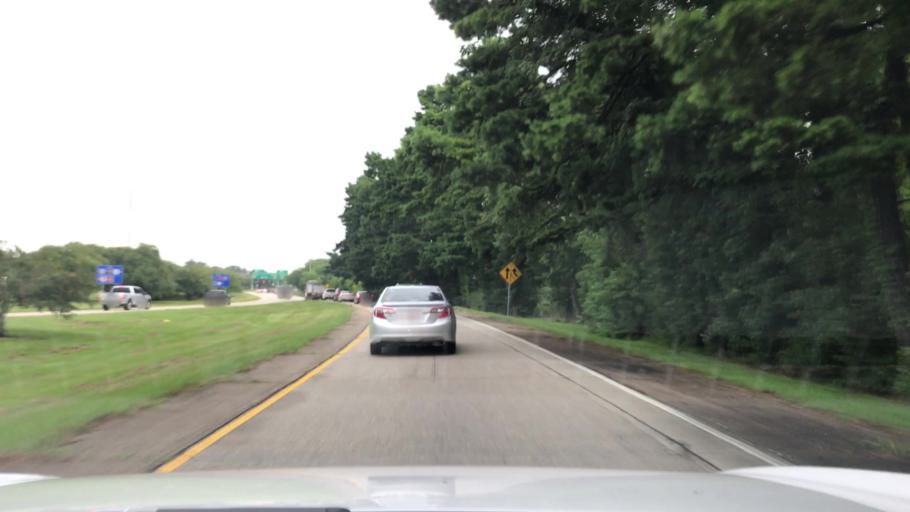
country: US
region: Louisiana
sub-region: East Baton Rouge Parish
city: Brownsfield
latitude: 30.5175
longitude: -91.1582
